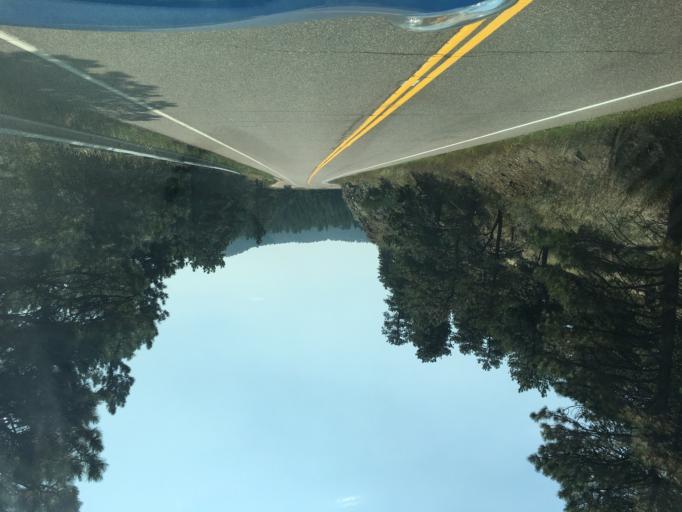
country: US
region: Colorado
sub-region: Jefferson County
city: Genesee
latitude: 39.7090
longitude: -105.2651
